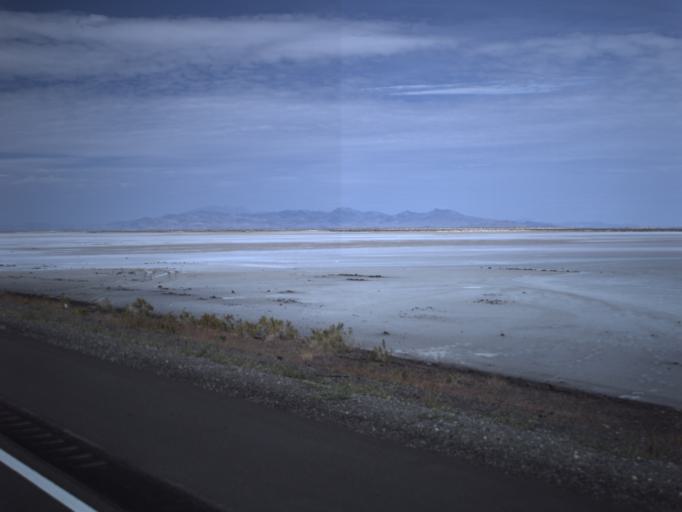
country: US
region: Utah
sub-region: Tooele County
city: Wendover
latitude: 40.7301
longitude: -113.4285
